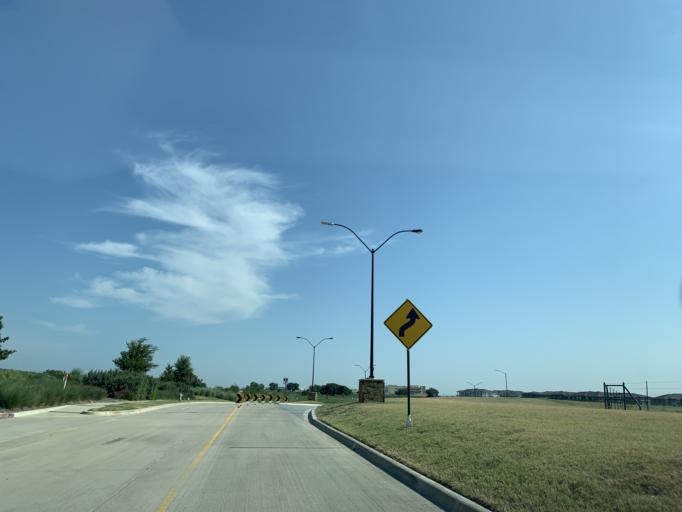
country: US
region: Texas
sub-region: Tarrant County
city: Keller
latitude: 32.9219
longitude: -97.3126
